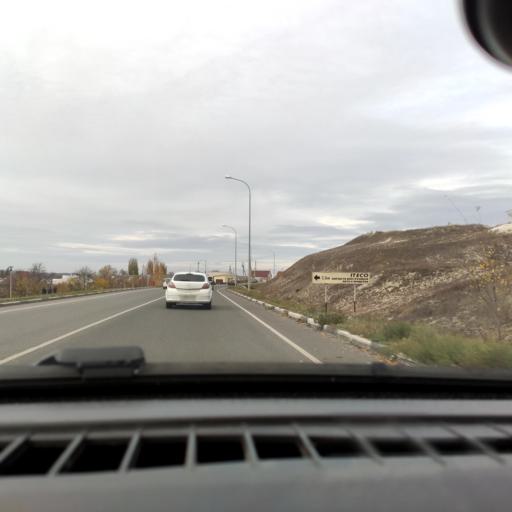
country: RU
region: Belgorod
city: Alekseyevka
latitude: 50.6412
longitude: 38.6614
